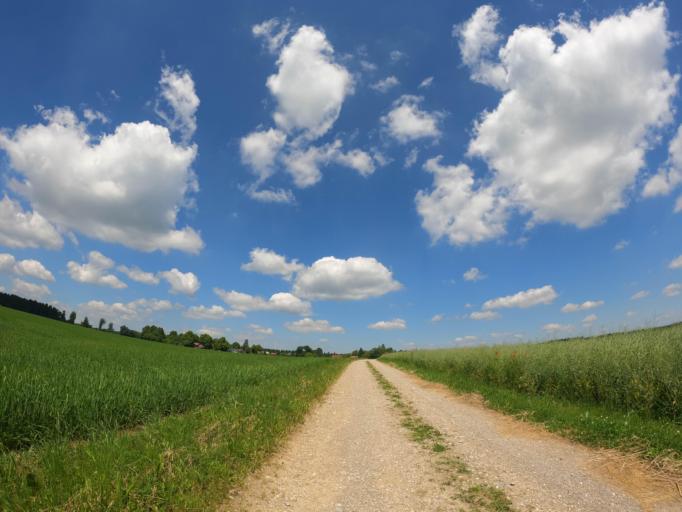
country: DE
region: Bavaria
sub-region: Upper Bavaria
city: Oberhaching
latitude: 47.9871
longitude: 11.5650
